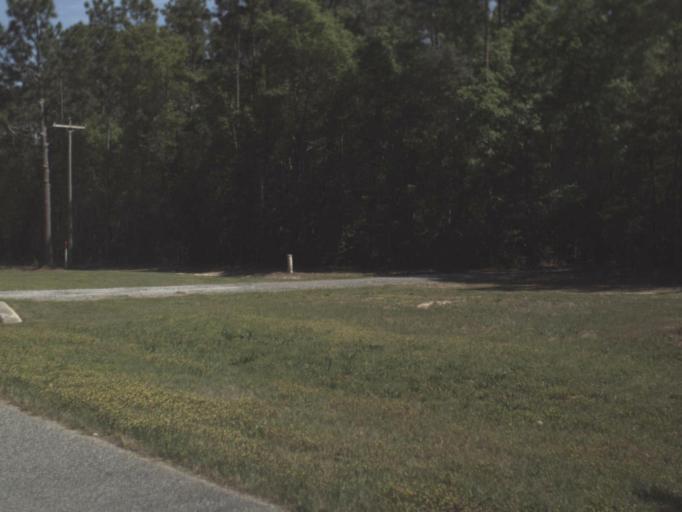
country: US
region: Florida
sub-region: Okaloosa County
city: Crestview
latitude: 30.7244
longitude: -86.6965
